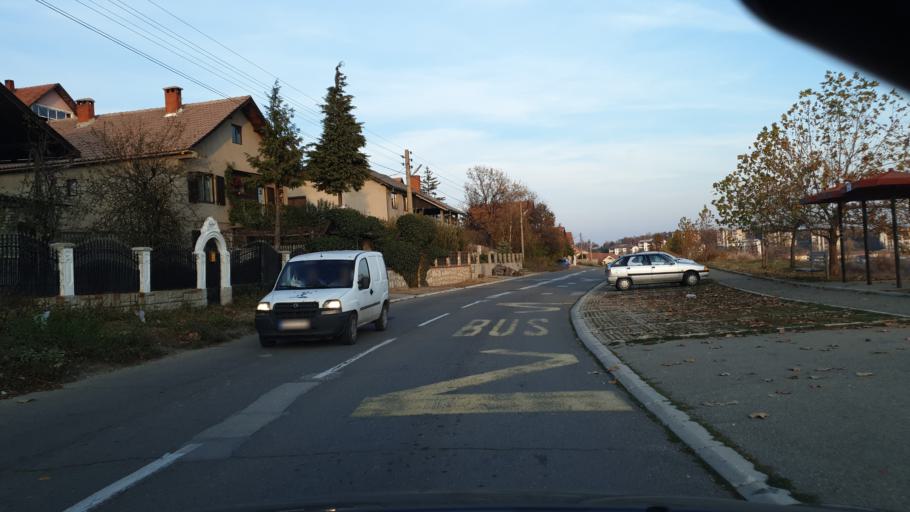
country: RS
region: Central Serbia
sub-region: Borski Okrug
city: Bor
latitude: 44.0578
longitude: 22.0860
